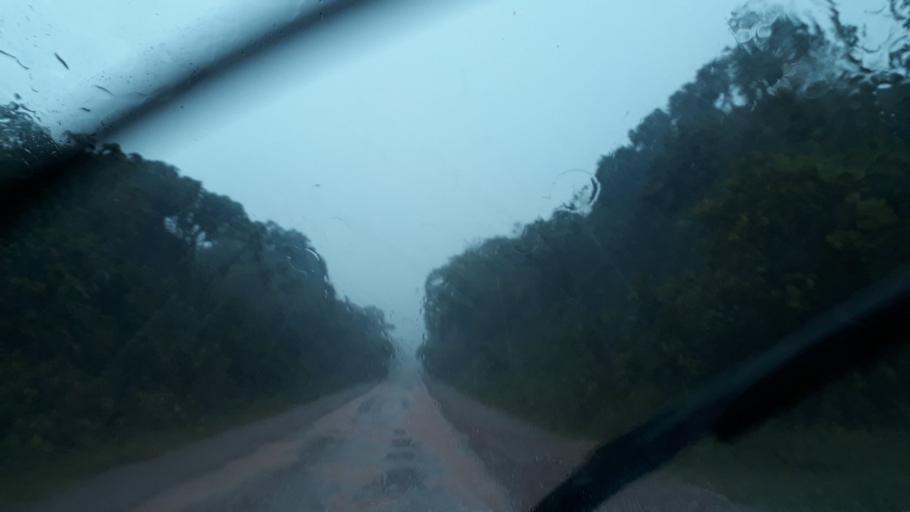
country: CD
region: Eastern Province
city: Kisangani
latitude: 0.4807
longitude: 25.5912
